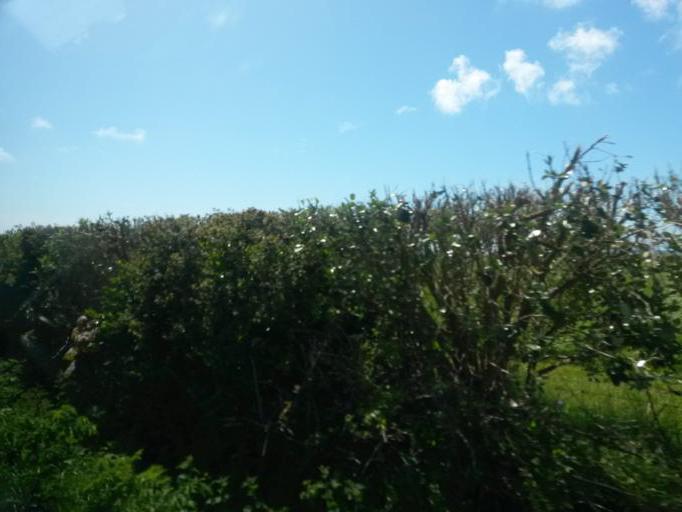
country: IE
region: Munster
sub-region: Waterford
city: Dunmore East
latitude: 52.1597
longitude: -6.8945
